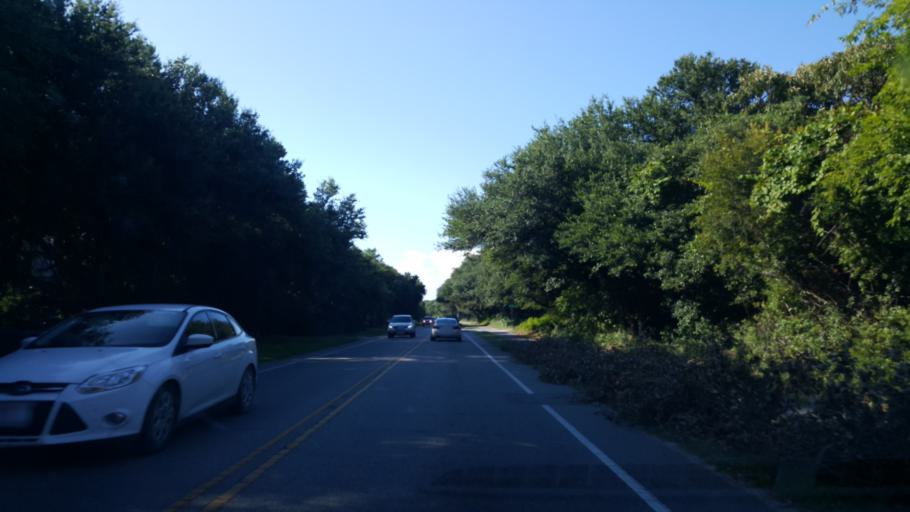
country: US
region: North Carolina
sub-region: Dare County
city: Southern Shores
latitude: 36.1377
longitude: -75.7361
